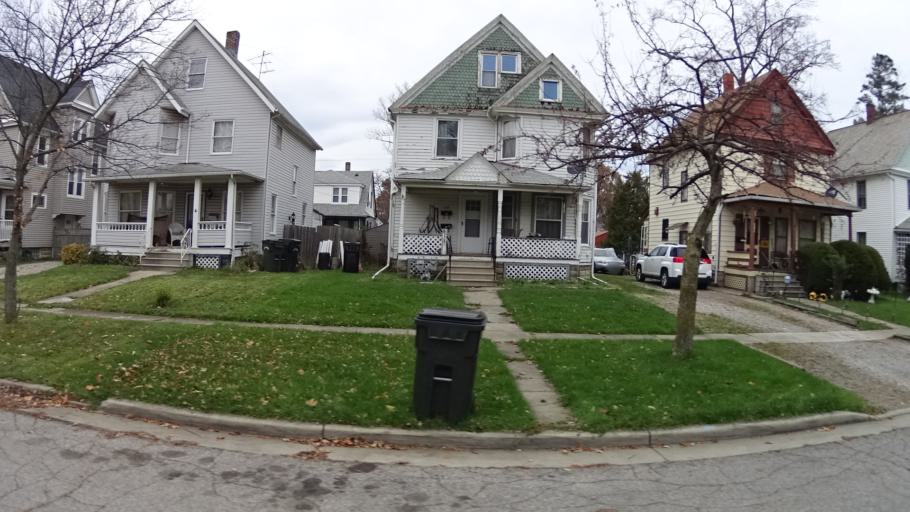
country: US
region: Ohio
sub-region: Lorain County
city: Elyria
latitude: 41.3551
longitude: -82.1097
